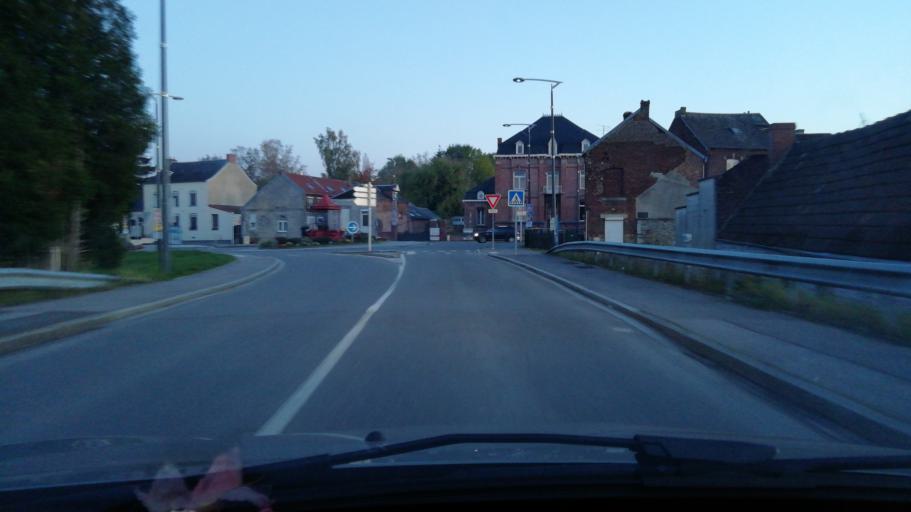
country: FR
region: Nord-Pas-de-Calais
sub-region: Departement du Nord
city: Marpent
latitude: 50.2919
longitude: 4.0790
